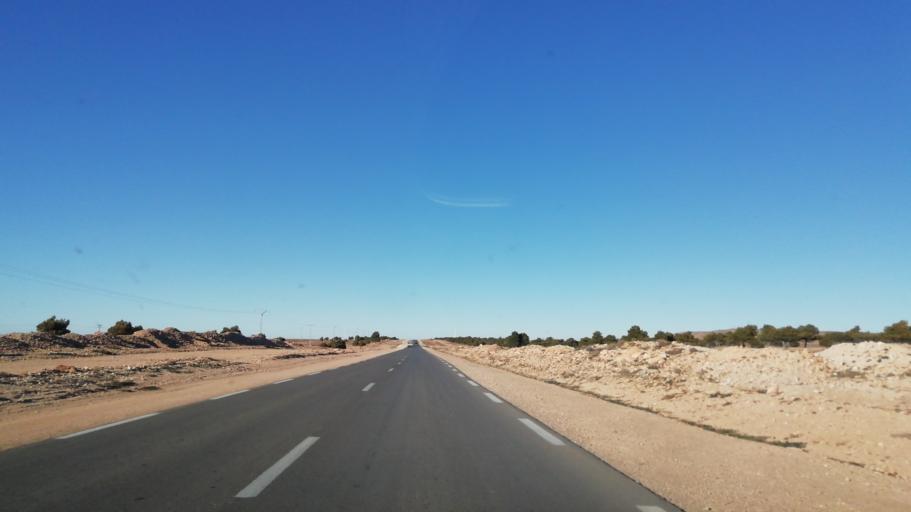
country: DZ
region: Tlemcen
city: Sebdou
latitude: 34.2377
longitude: -1.2567
